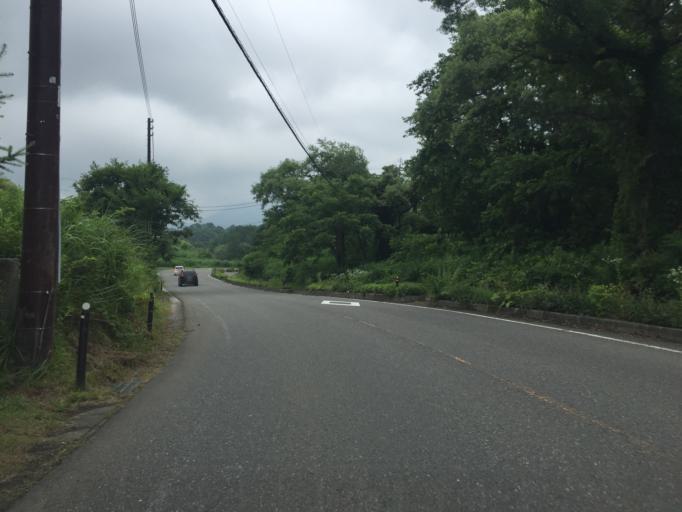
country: JP
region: Fukushima
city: Inawashiro
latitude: 37.6650
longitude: 140.0786
